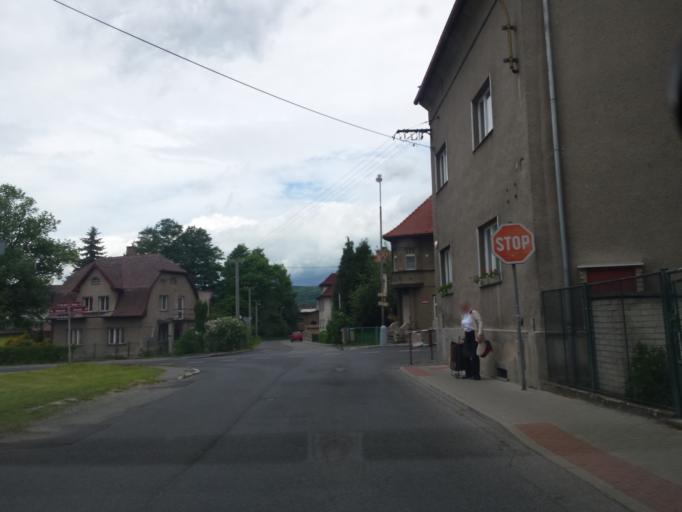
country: CZ
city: Novy Bor
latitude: 50.7620
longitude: 14.5588
